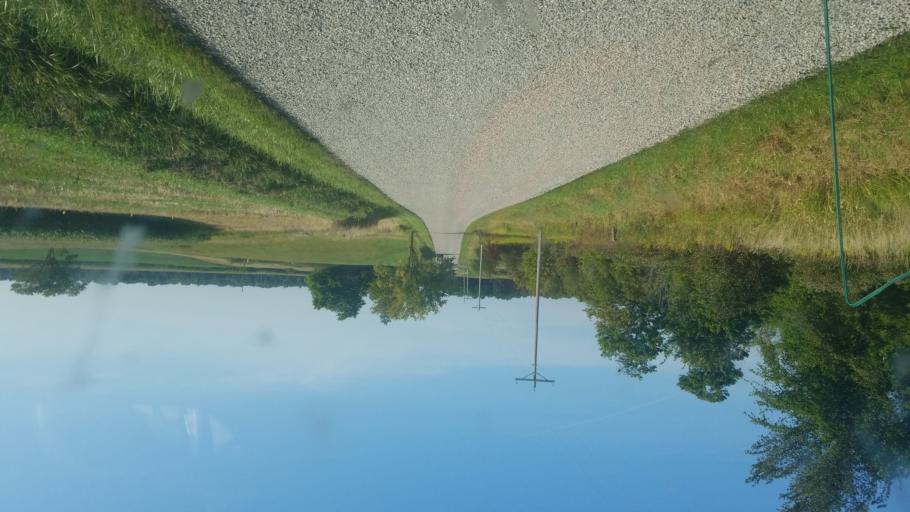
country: US
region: Ohio
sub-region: Ashland County
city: Ashland
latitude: 40.9562
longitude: -82.3399
